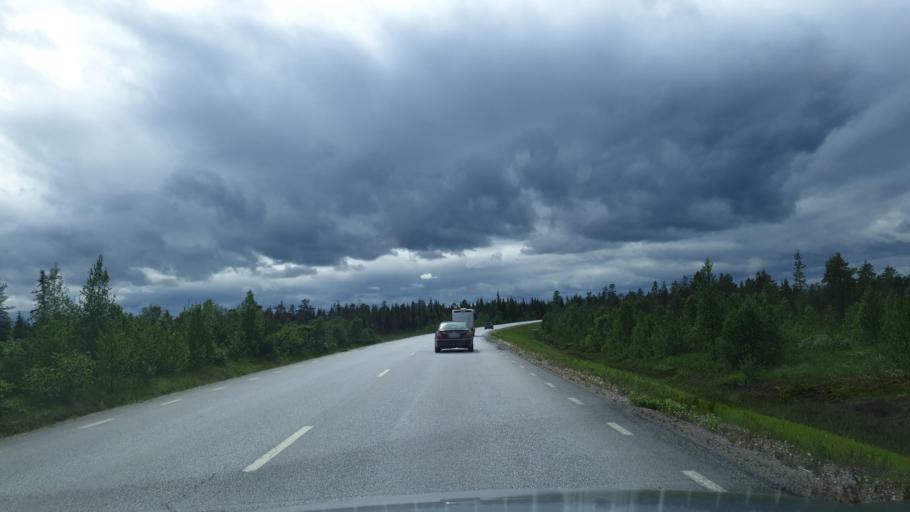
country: SE
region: Norrbotten
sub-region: Jokkmokks Kommun
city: Jokkmokk
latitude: 67.0203
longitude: 19.9178
